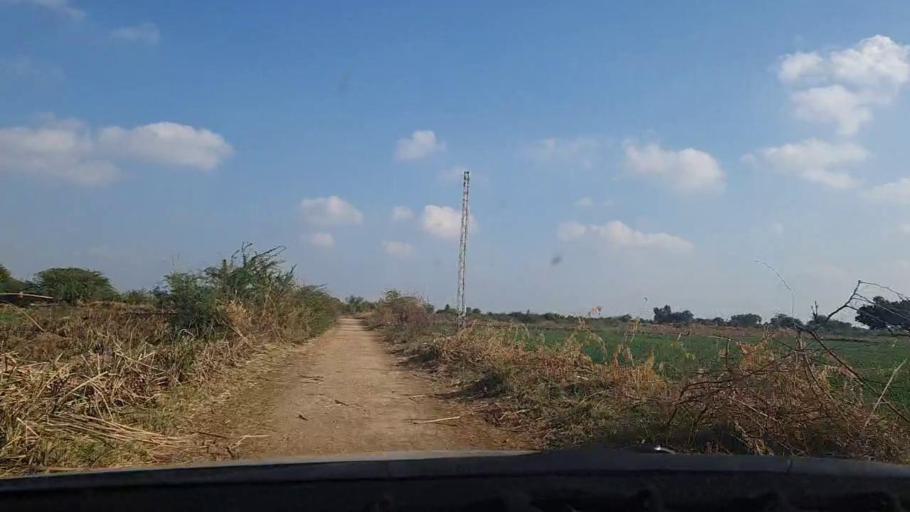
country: PK
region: Sindh
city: Tando Mittha Khan
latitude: 25.8867
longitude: 69.3008
